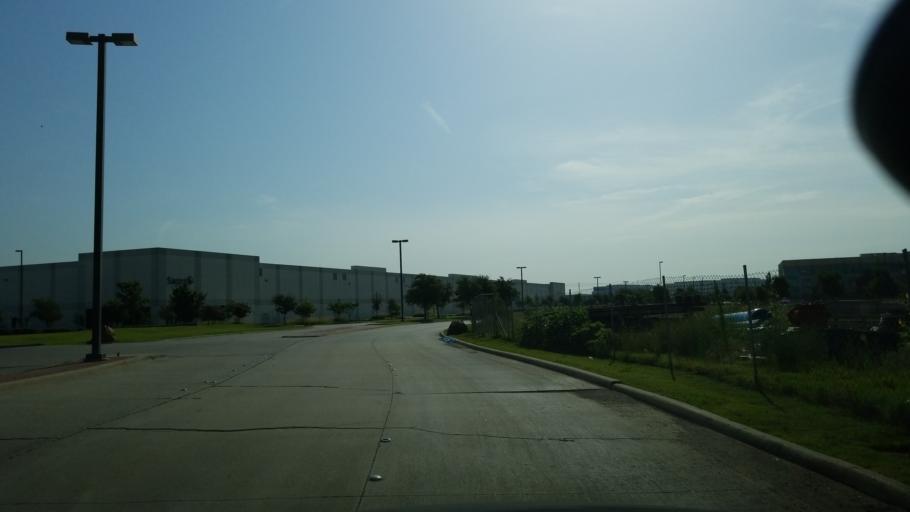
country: US
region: Texas
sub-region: Dallas County
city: Coppell
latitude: 32.9296
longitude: -96.9979
